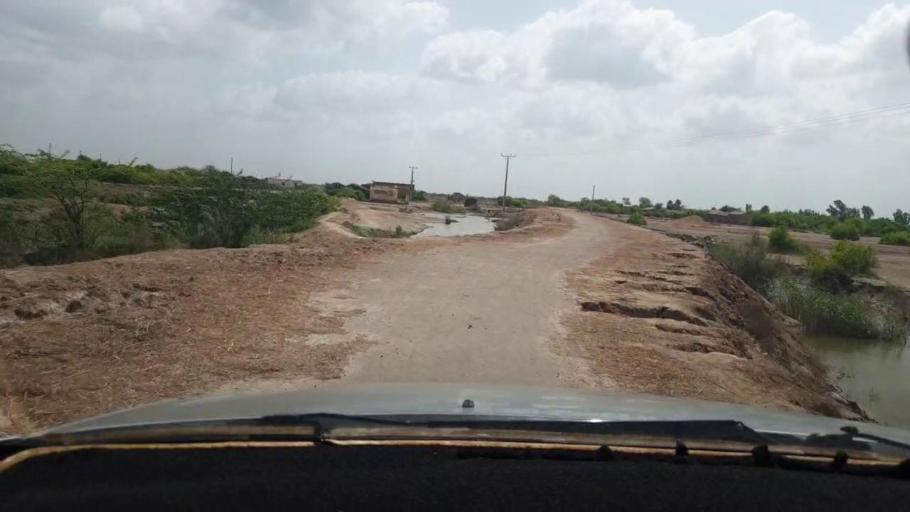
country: PK
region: Sindh
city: Tando Bago
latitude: 24.7208
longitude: 69.1400
